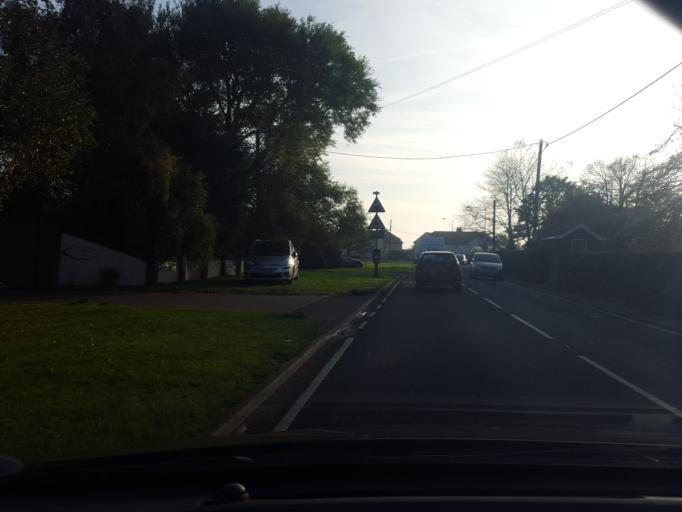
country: GB
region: England
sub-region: Essex
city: Frinton-on-Sea
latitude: 51.8331
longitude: 1.2100
